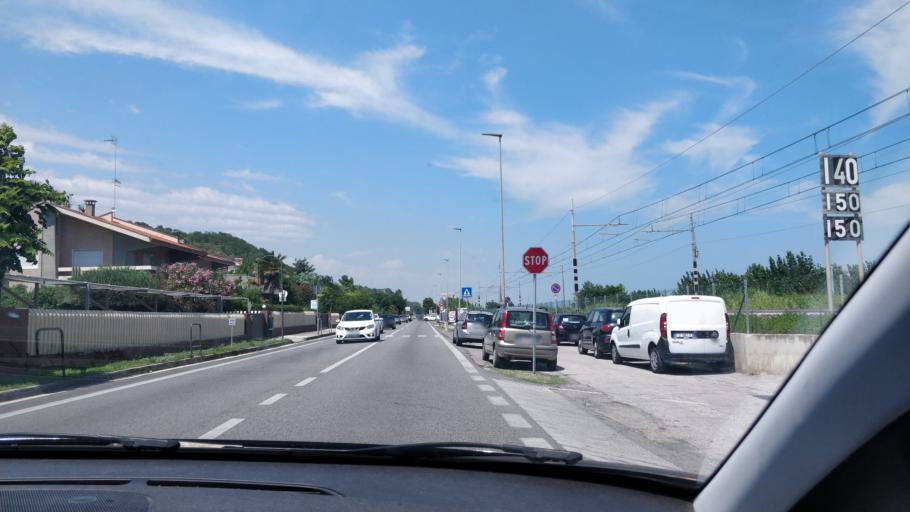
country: IT
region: Abruzzo
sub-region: Provincia di Chieti
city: Tollo
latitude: 42.3807
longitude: 14.3653
